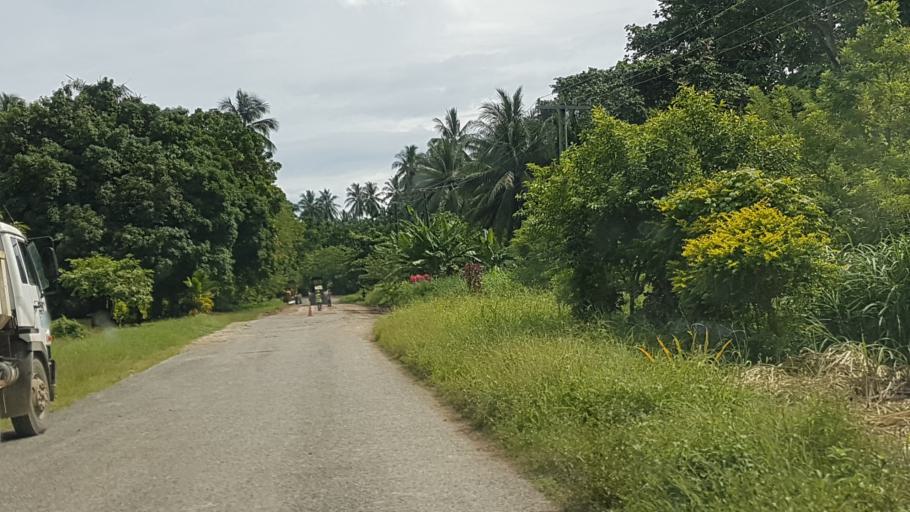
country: PG
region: Madang
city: Madang
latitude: -4.8728
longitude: 145.8014
